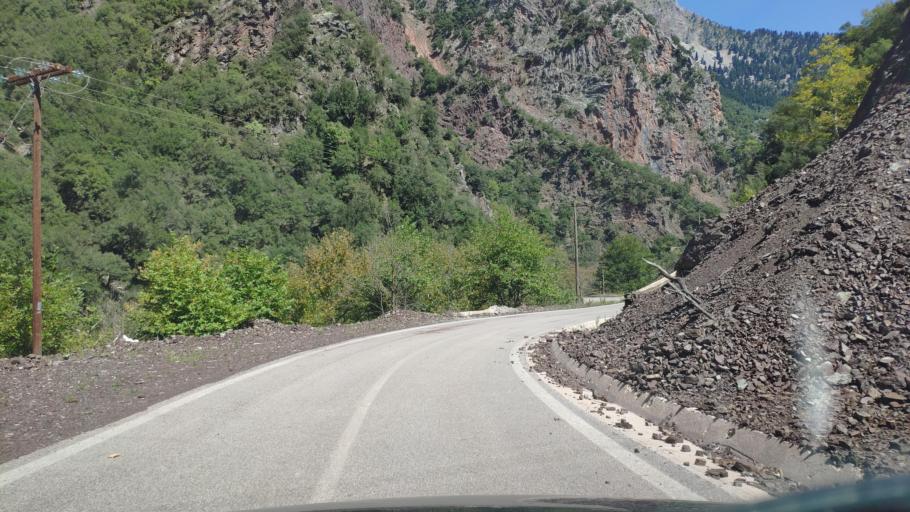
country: GR
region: Central Greece
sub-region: Nomos Evrytanias
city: Kerasochori
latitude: 39.1323
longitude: 21.6317
